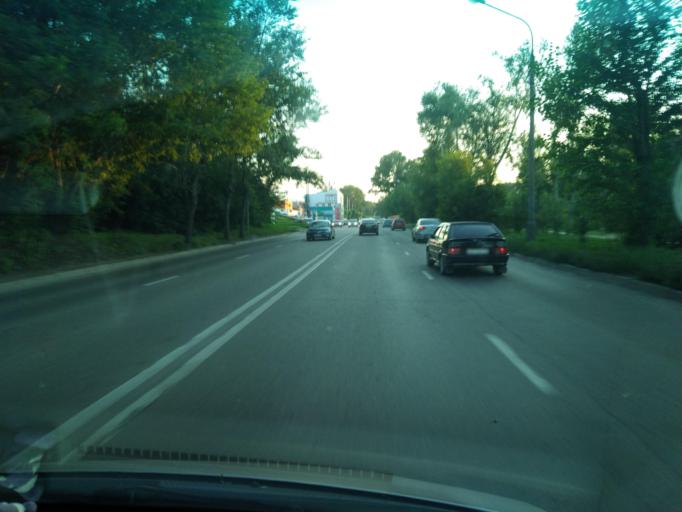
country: RU
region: Krasnoyarskiy
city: Krasnoyarsk
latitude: 55.9860
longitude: 92.8938
